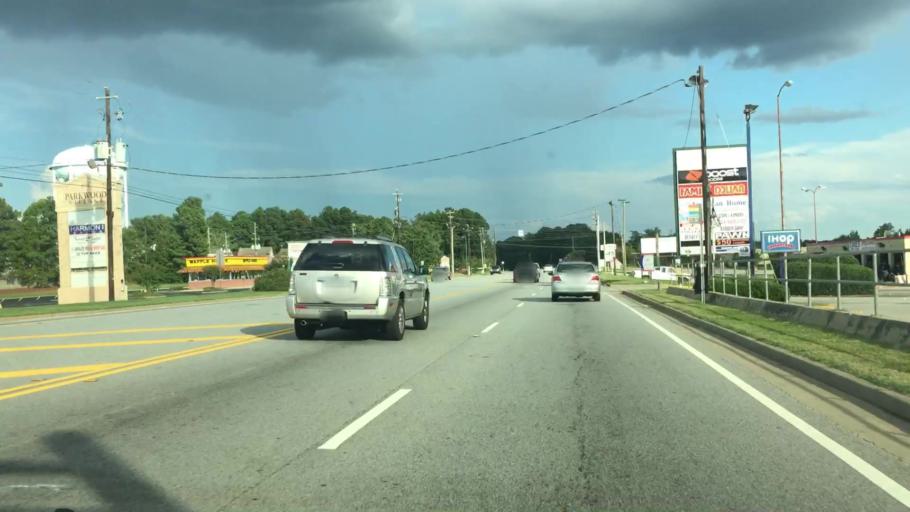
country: US
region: Georgia
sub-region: Clayton County
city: Riverdale
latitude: 33.5491
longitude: -84.4137
